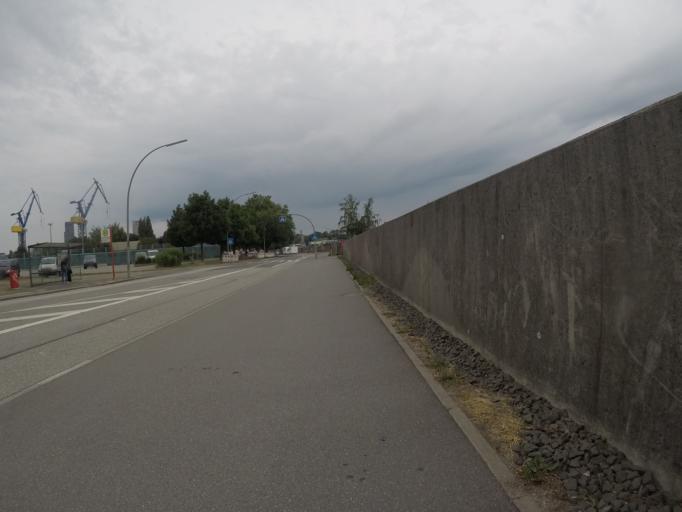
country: DE
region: Hamburg
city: St. Pauli
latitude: 53.5395
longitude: 9.9658
